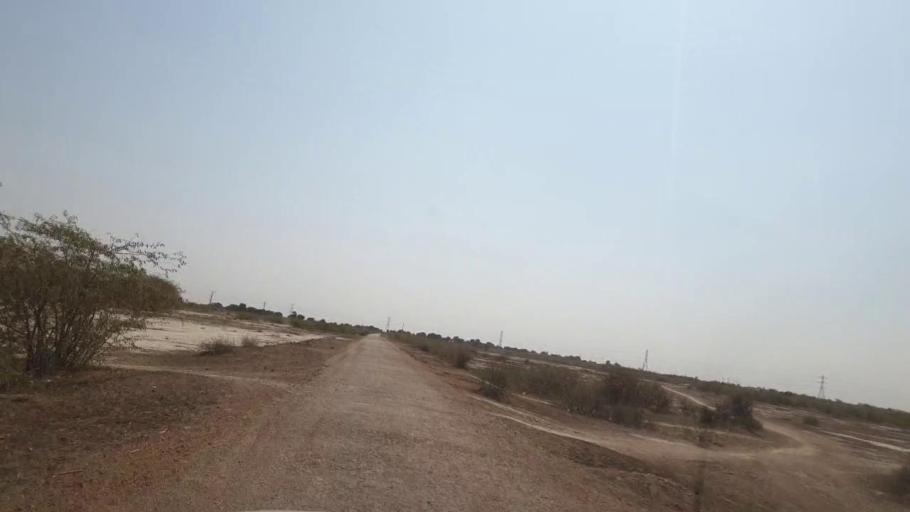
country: PK
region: Sindh
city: Nabisar
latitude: 25.0716
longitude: 69.5487
